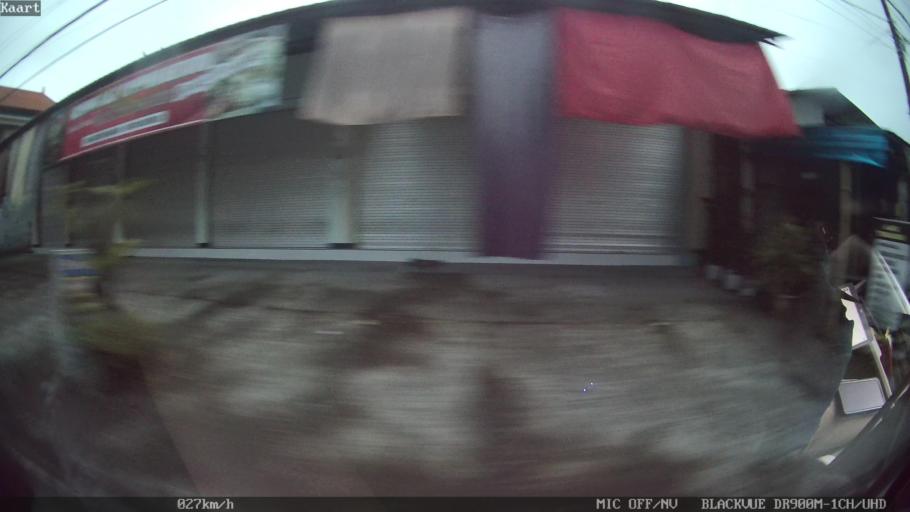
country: ID
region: Bali
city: Banjar Buahan
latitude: -8.4051
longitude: 115.2465
